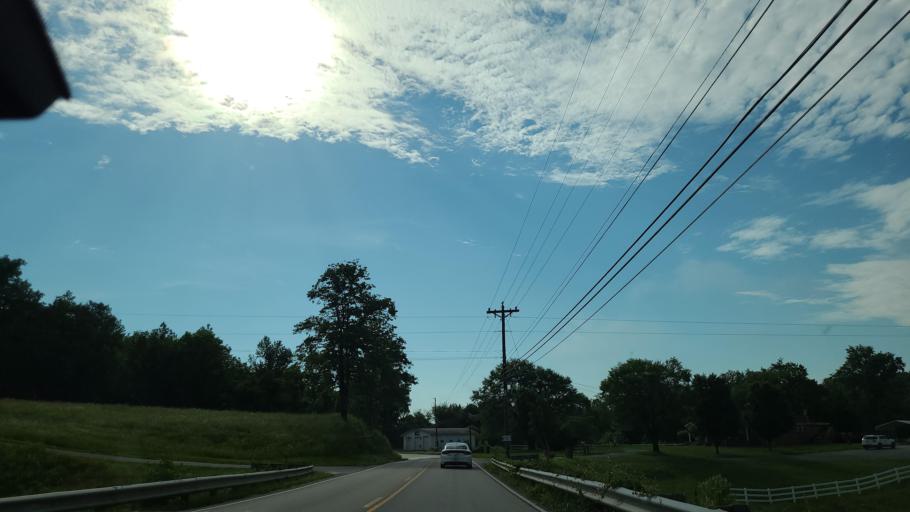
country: US
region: Kentucky
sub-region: Whitley County
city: Williamsburg
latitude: 36.7397
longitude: -84.0834
